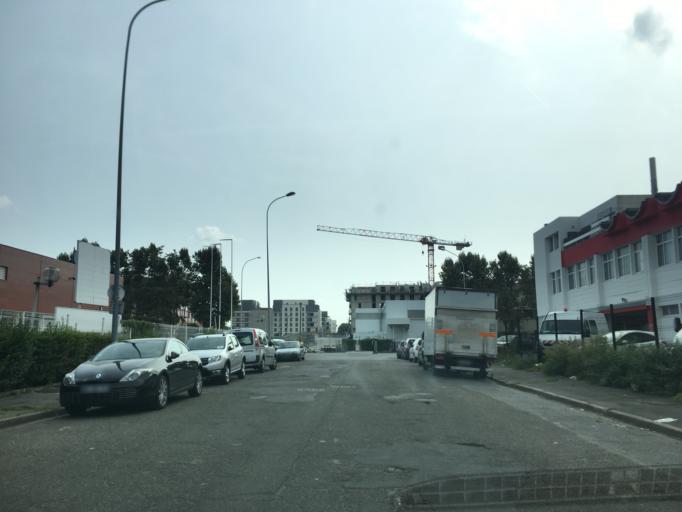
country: FR
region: Ile-de-France
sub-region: Departement du Val-de-Marne
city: Maisons-Alfort
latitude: 48.7885
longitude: 2.4368
